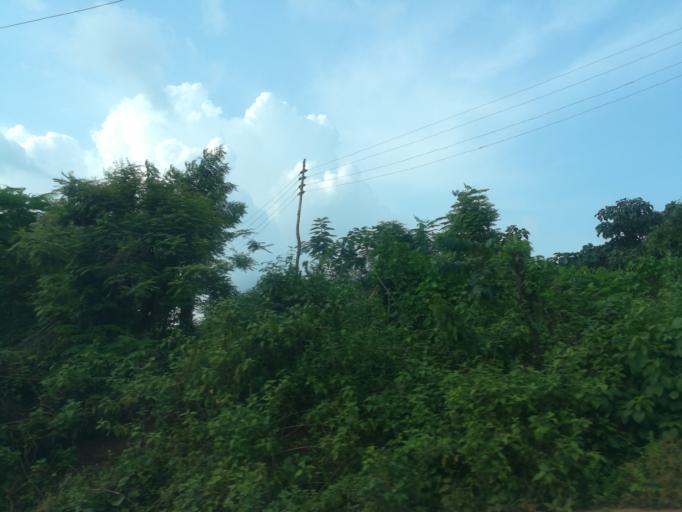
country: NG
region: Oyo
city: Moniya
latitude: 7.5260
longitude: 3.9255
